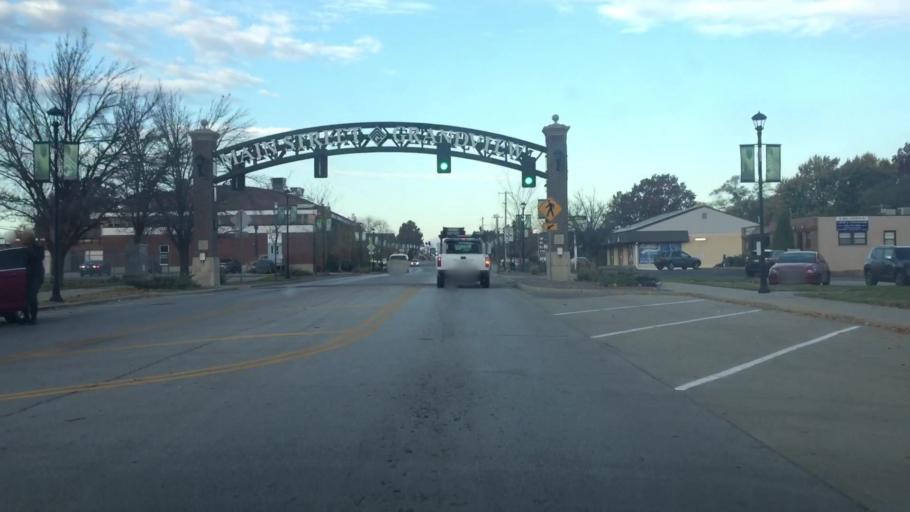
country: US
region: Missouri
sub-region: Jackson County
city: Grandview
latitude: 38.8892
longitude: -94.5315
